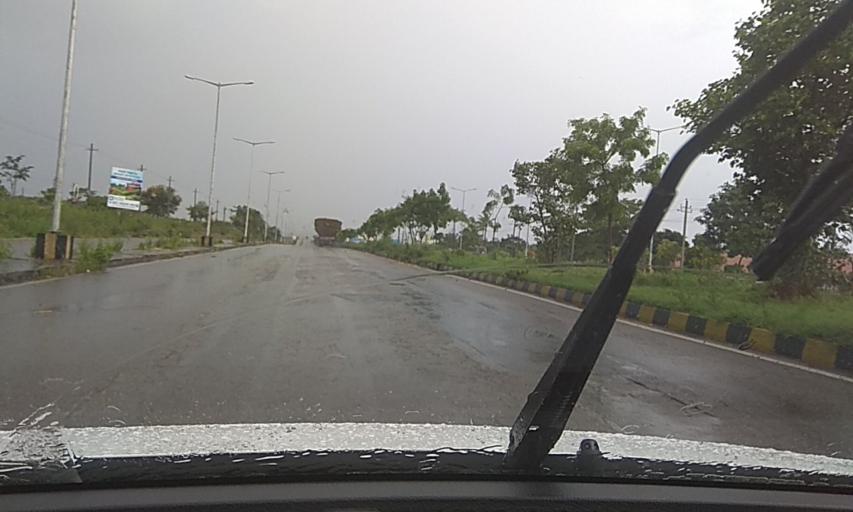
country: IN
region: Karnataka
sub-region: Mysore
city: Mysore
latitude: 12.3462
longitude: 76.6726
